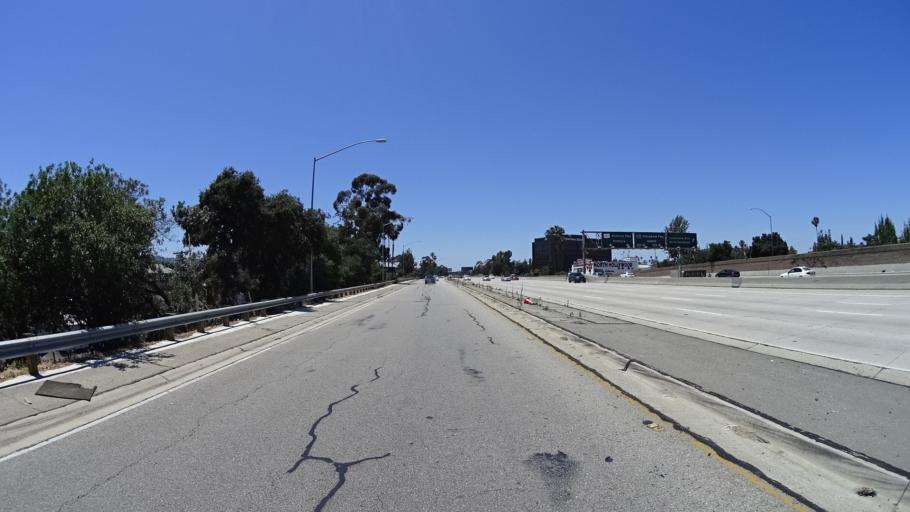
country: US
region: California
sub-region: Los Angeles County
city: Universal City
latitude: 34.1530
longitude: -118.3652
